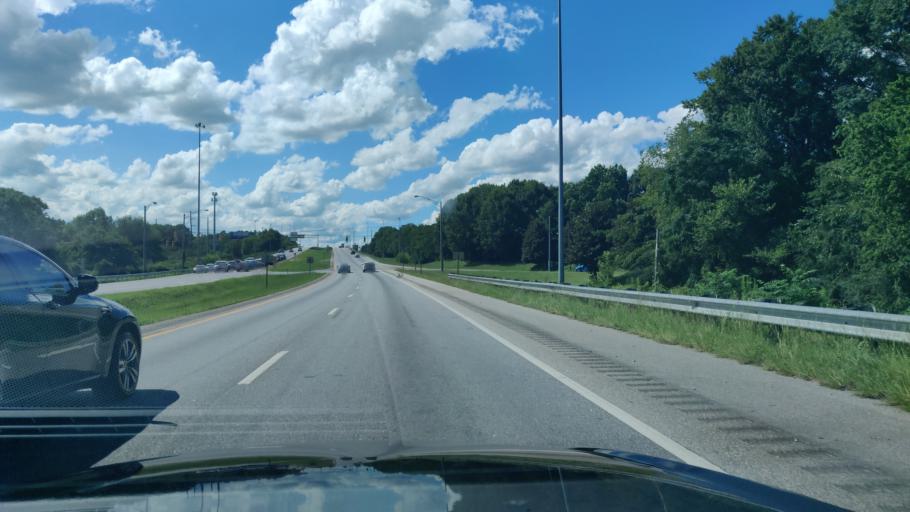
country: US
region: Alabama
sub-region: Russell County
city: Phenix City
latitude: 32.4890
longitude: -85.0339
